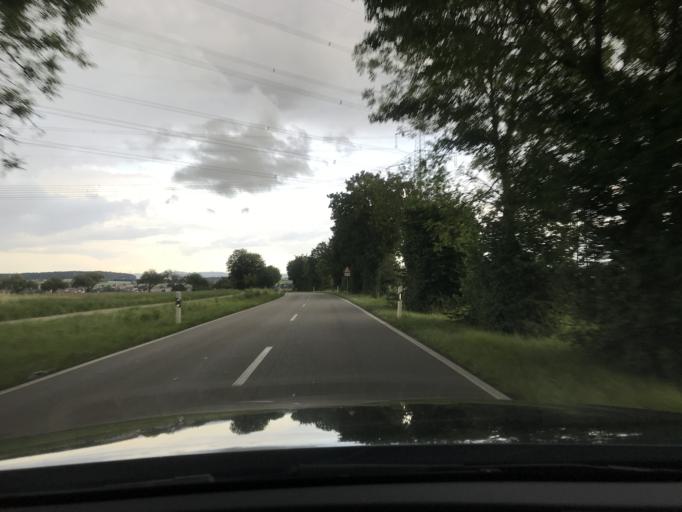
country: DE
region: Baden-Wuerttemberg
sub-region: Regierungsbezirk Stuttgart
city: Affalterbach
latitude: 48.8871
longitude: 9.2968
